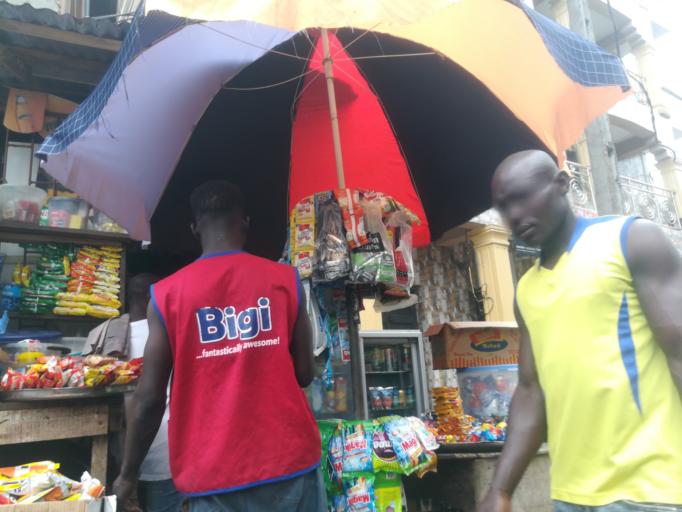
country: NG
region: Lagos
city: Lagos
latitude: 6.4588
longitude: 3.3819
